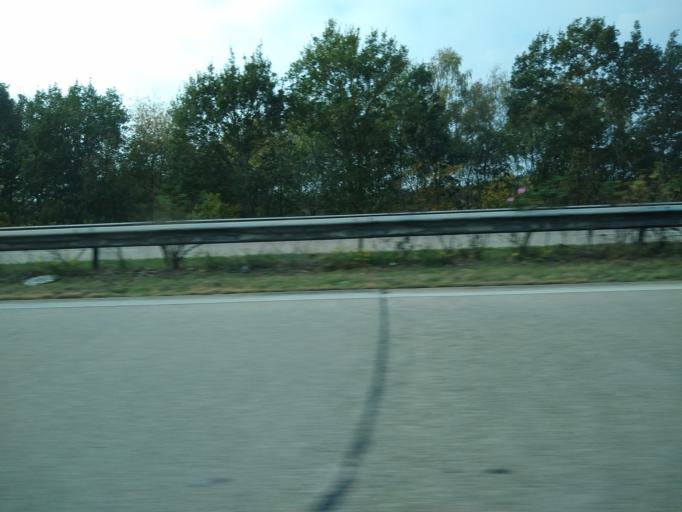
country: DE
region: Lower Saxony
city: Oldenburg
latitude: 53.1266
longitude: 8.2758
